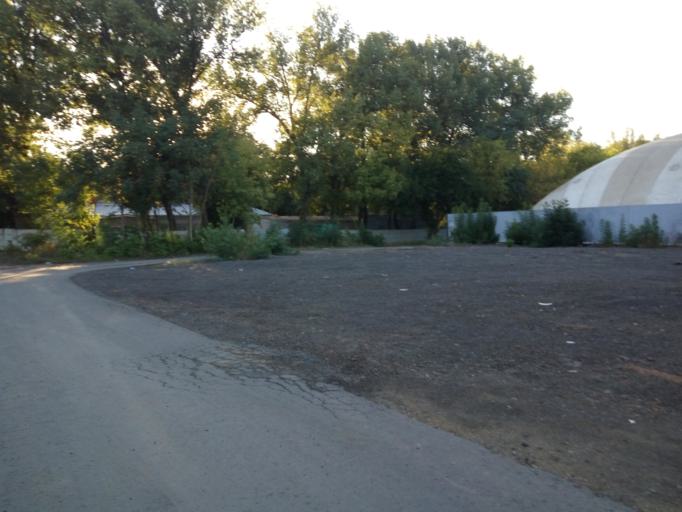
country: RU
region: Rostov
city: Rostov-na-Donu
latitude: 47.2445
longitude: 39.7583
